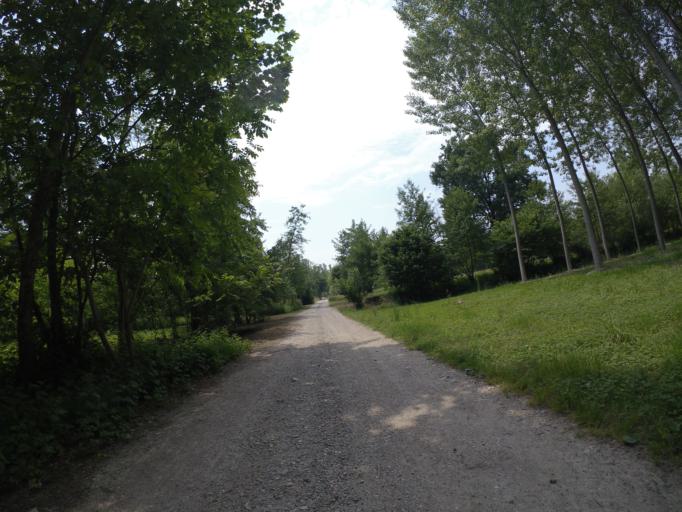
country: IT
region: Friuli Venezia Giulia
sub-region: Provincia di Udine
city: Bertiolo
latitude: 45.9232
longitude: 13.0410
